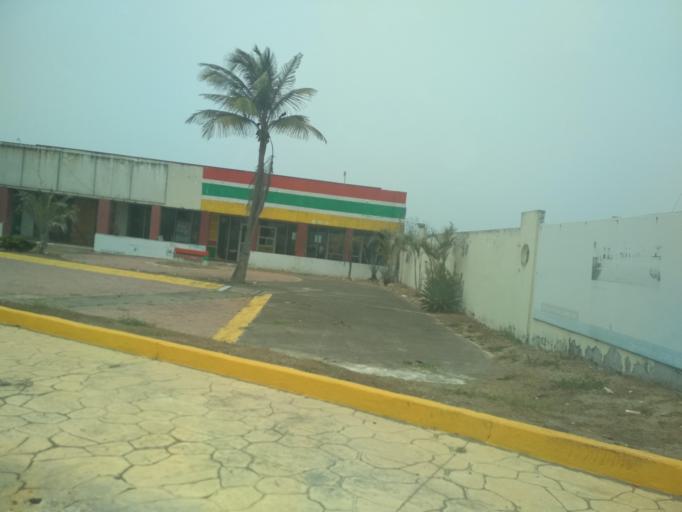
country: MX
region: Veracruz
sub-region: Alvarado
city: Playa de la Libertad
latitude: 19.0567
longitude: -96.0608
